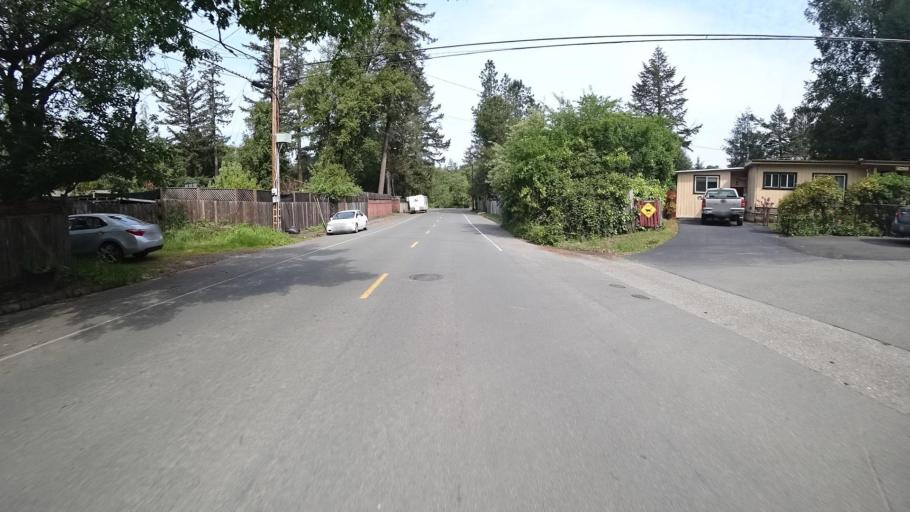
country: US
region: California
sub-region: Humboldt County
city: Redway
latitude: 40.1200
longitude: -123.8303
